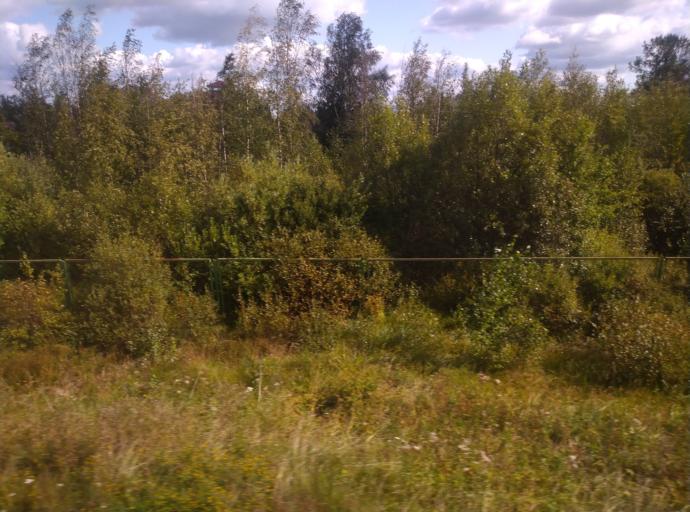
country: RU
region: Leningrad
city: Ul'yanovka
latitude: 59.6455
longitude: 30.7448
